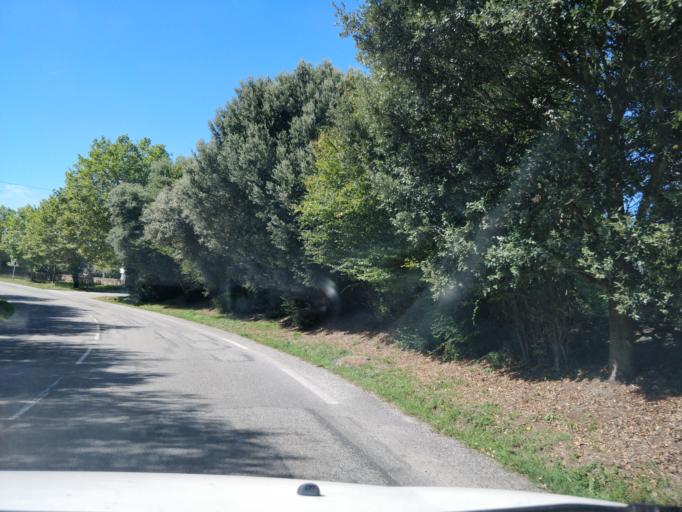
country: FR
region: Brittany
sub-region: Departement du Morbihan
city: Saint-Philibert
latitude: 47.5789
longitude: -3.0002
